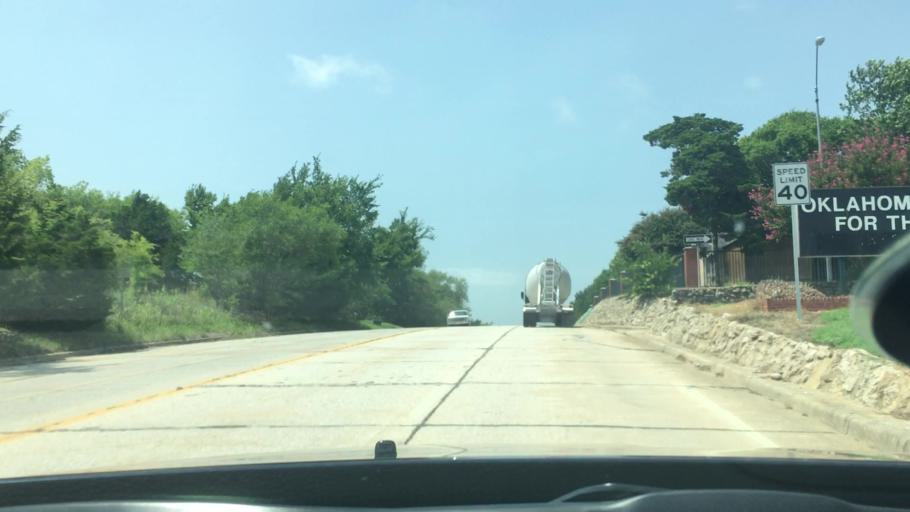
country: US
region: Oklahoma
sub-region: Murray County
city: Sulphur
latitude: 34.5109
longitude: -96.9520
